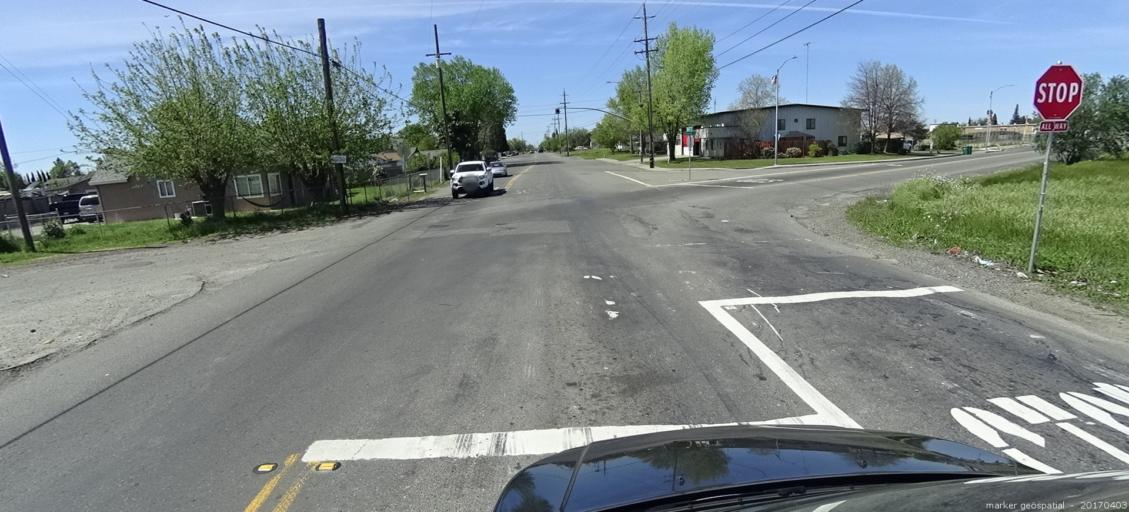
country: US
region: California
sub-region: Sacramento County
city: Rio Linda
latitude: 38.6474
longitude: -121.4345
